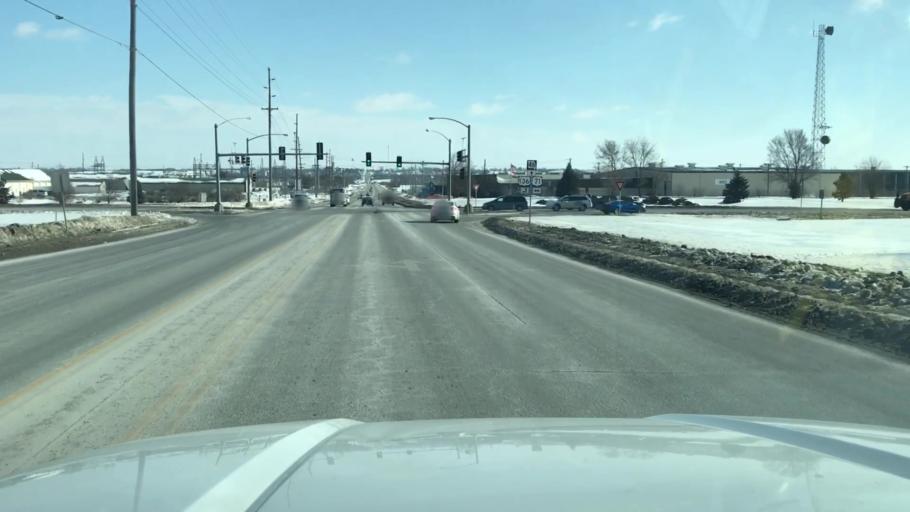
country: US
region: Missouri
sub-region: Nodaway County
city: Maryville
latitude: 40.3453
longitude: -94.8532
